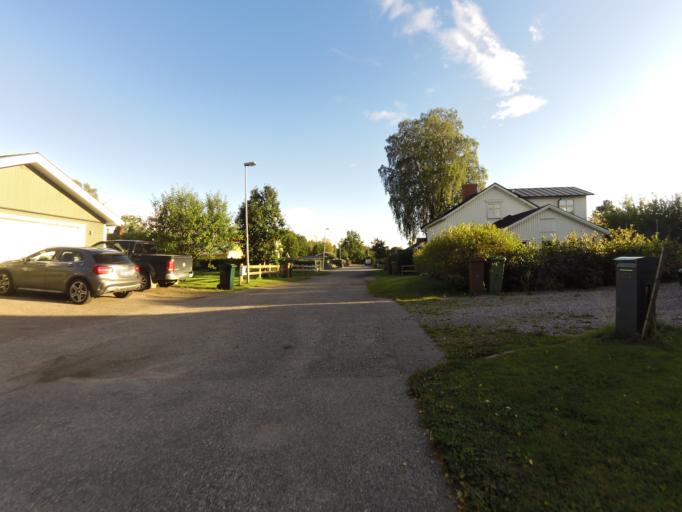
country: SE
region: Gaevleborg
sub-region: Gavle Kommun
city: Gavle
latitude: 60.7242
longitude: 17.1694
